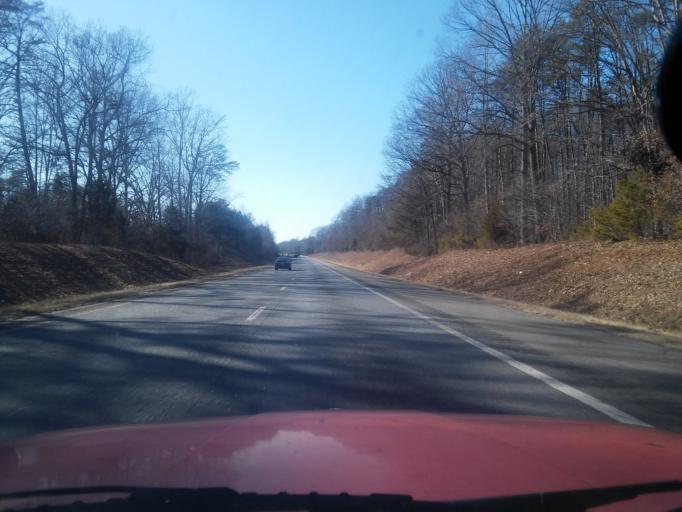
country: US
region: Virginia
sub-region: Fluvanna County
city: Lake Monticello
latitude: 37.9974
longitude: -78.2919
